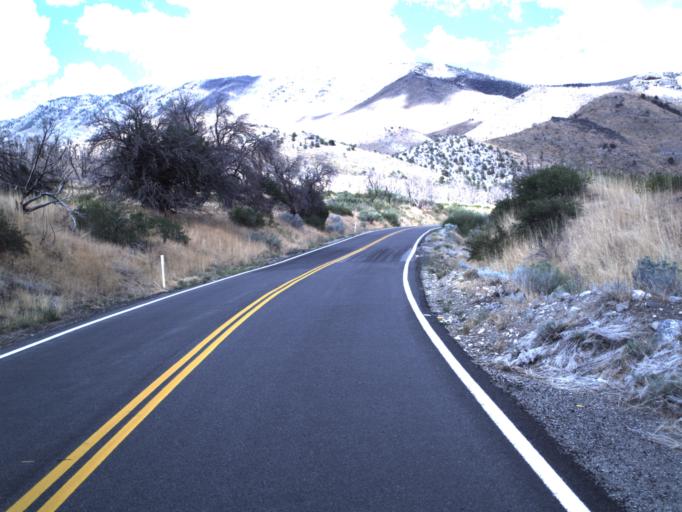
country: US
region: Utah
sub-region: Tooele County
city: Grantsville
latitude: 40.3395
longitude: -112.6093
